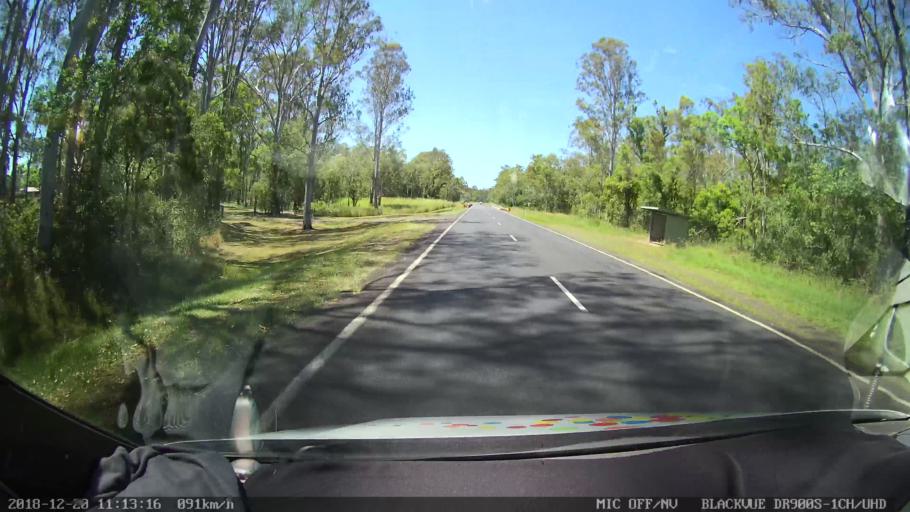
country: AU
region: New South Wales
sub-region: Richmond Valley
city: Casino
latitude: -28.9854
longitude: 153.0100
